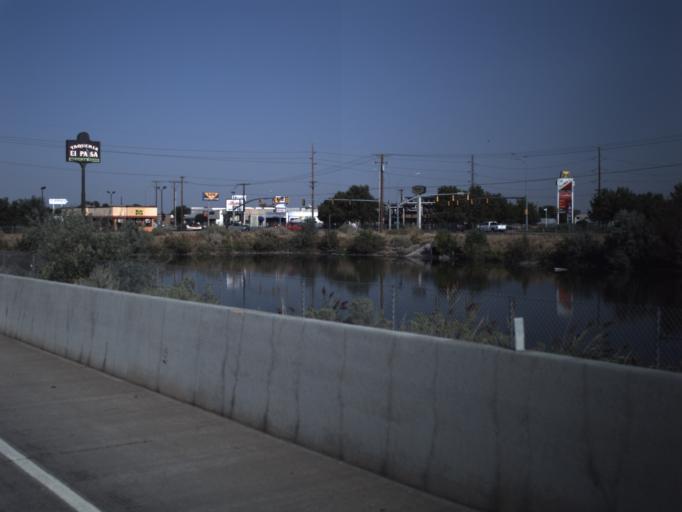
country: US
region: Utah
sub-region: Salt Lake County
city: South Salt Lake
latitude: 40.7247
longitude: -111.9151
